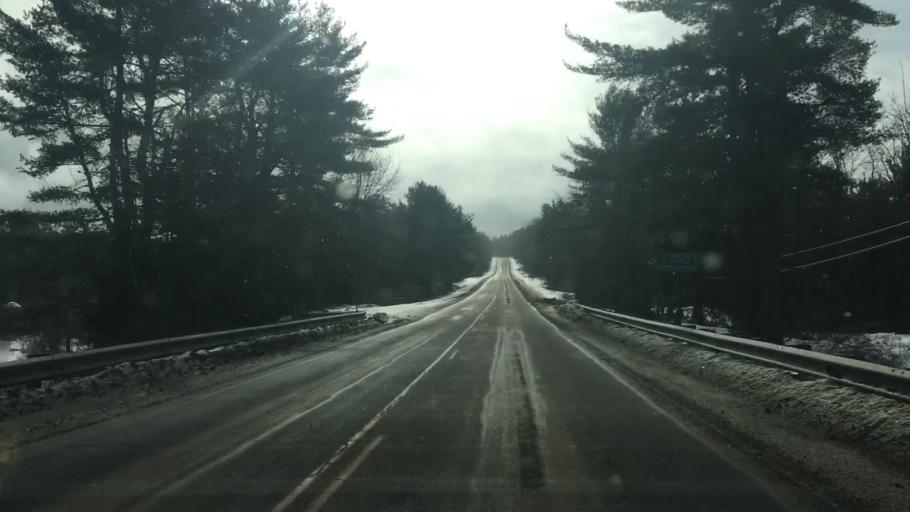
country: US
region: Maine
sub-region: Washington County
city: Calais
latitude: 45.0739
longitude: -67.3321
